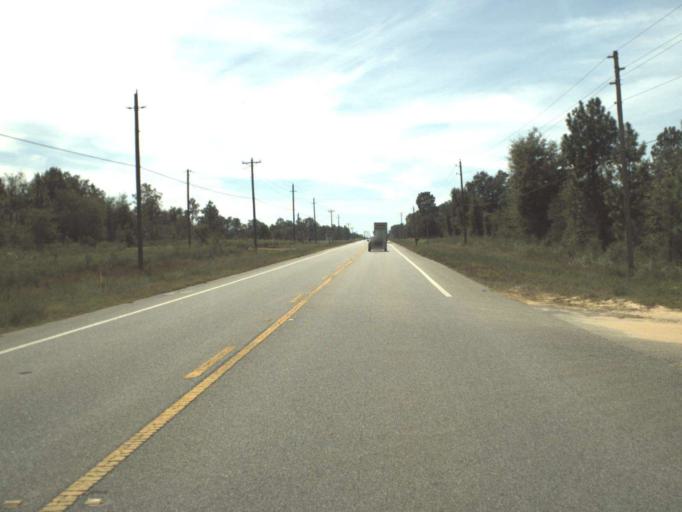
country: US
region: Florida
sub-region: Holmes County
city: Bonifay
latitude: 30.5350
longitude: -85.6409
